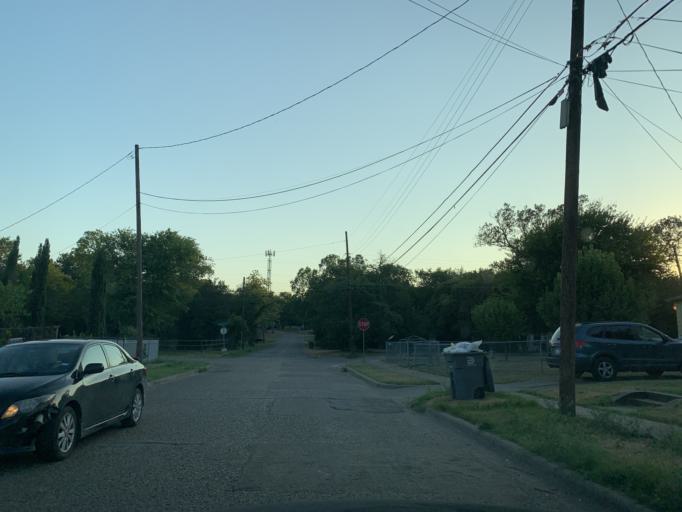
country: US
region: Texas
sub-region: Dallas County
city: Dallas
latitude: 32.7060
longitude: -96.8044
